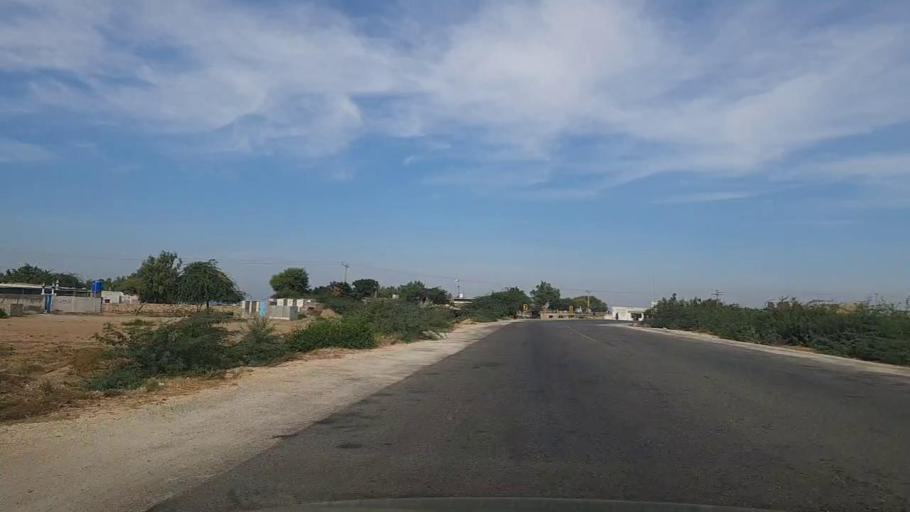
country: PK
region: Sindh
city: Daro Mehar
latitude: 24.9134
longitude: 68.0740
